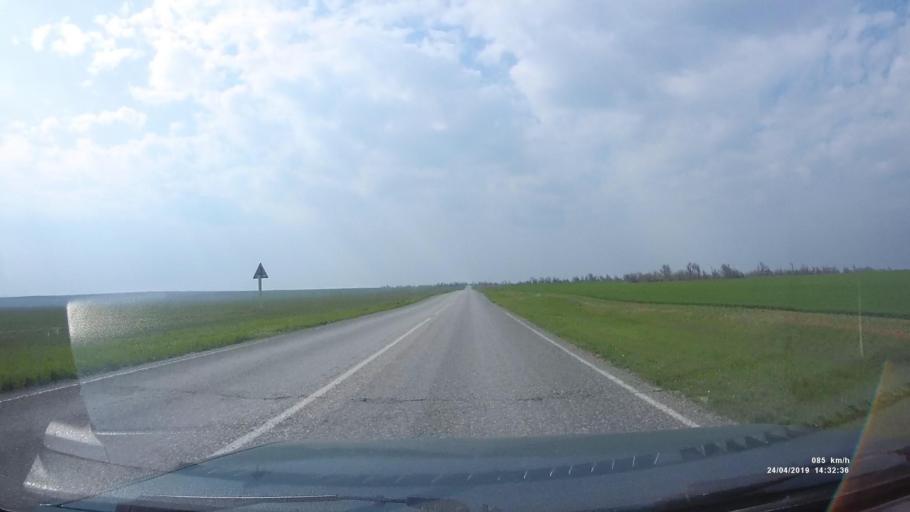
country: RU
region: Kalmykiya
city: Arshan'
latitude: 46.3659
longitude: 43.9665
